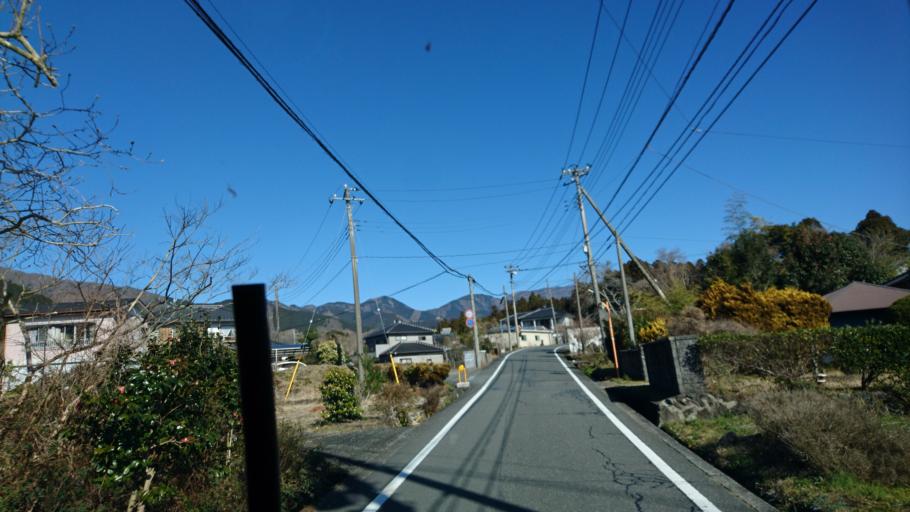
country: JP
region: Shizuoka
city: Fujinomiya
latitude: 35.3287
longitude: 138.5756
